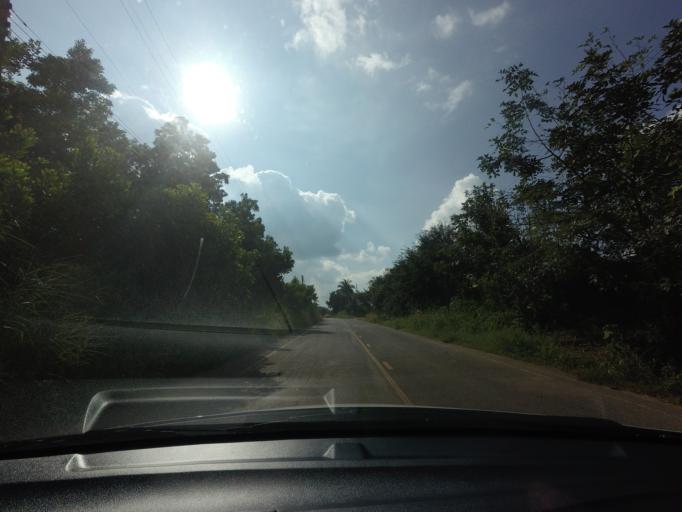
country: TH
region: Nakhon Ratchasima
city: Pak Chong
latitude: 14.5527
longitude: 101.6067
